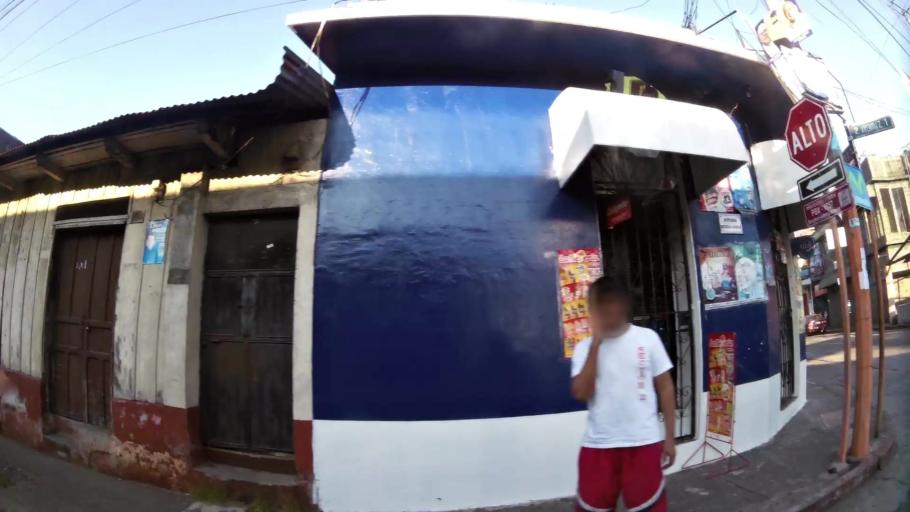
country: GT
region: Suchitepeque
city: Mazatenango
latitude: 14.5374
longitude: -91.5048
